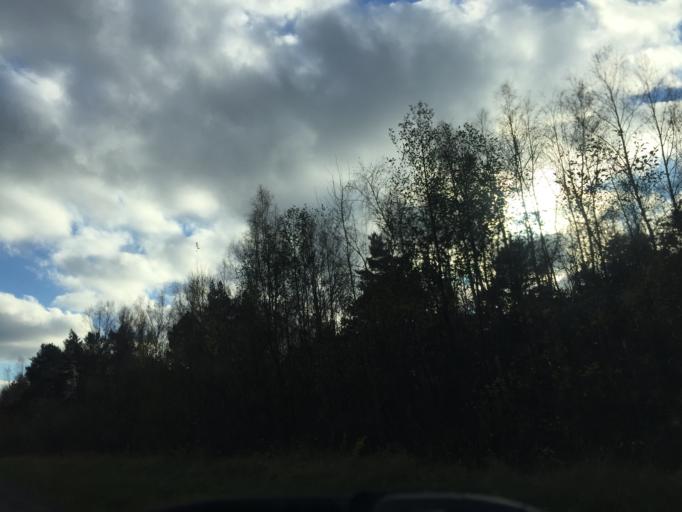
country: LV
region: Liepaja
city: Vec-Liepaja
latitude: 56.5803
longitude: 21.0390
